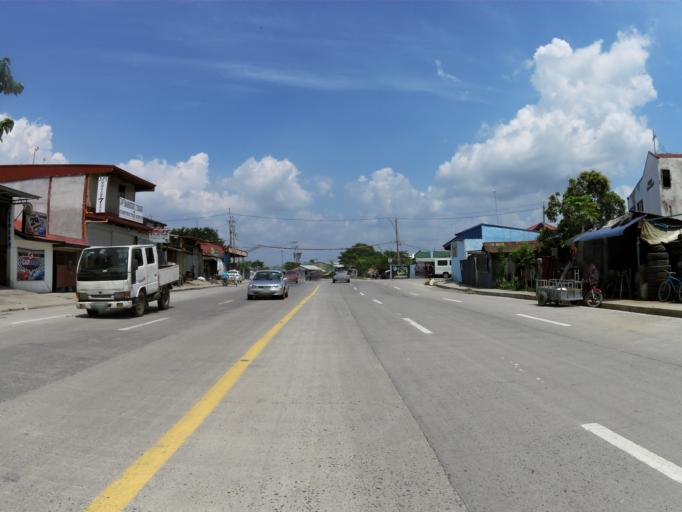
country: PH
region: Calabarzon
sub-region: Province of Rizal
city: Taytay
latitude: 14.5342
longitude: 121.1122
